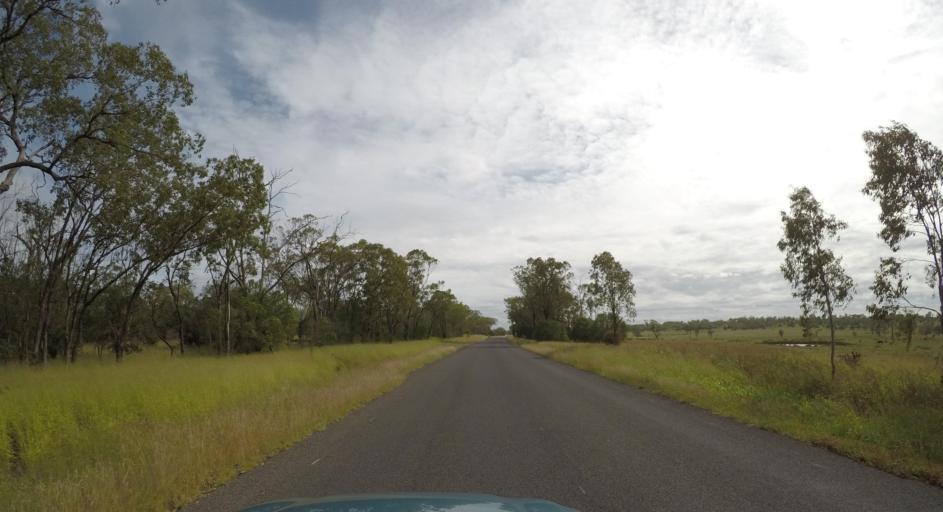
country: AU
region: Queensland
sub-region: Western Downs
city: Dalby
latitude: -27.0500
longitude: 151.3136
